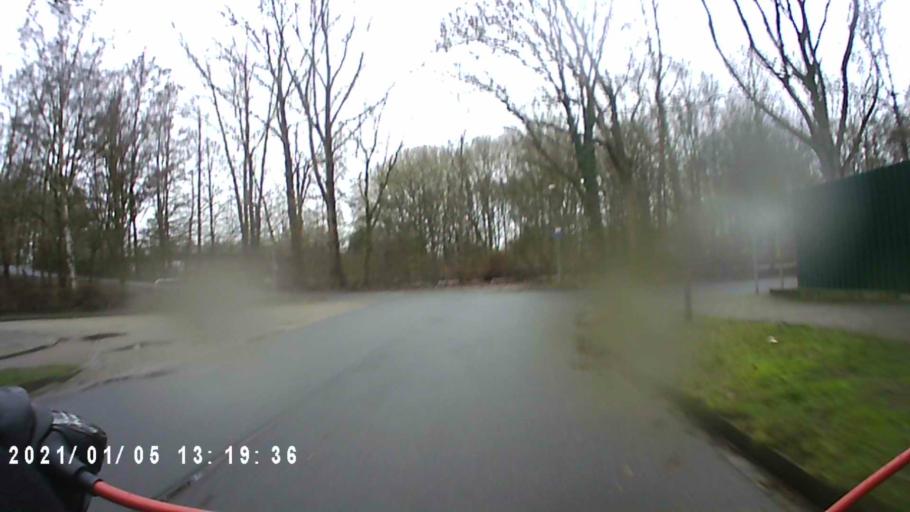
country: DE
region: Lower Saxony
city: Leer
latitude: 53.2359
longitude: 7.4381
